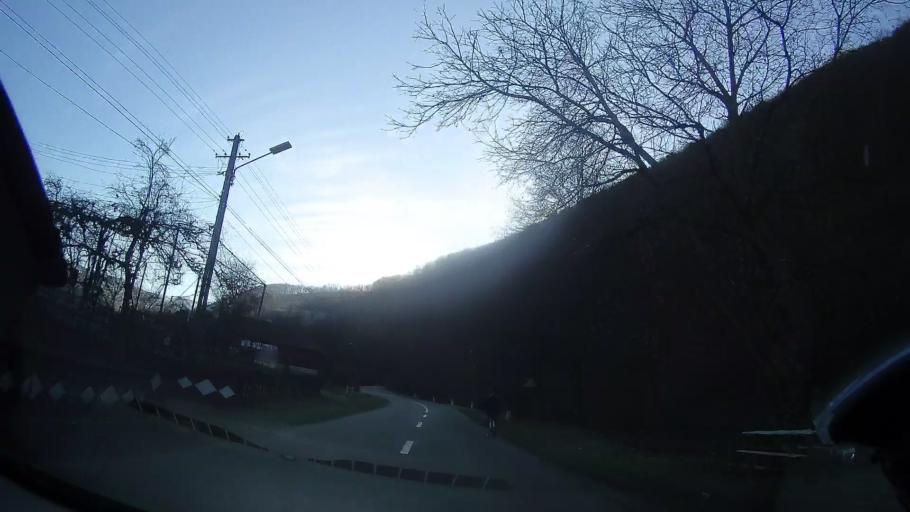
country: RO
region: Bihor
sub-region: Comuna Bulz
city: Bulz
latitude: 46.9109
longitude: 22.6766
